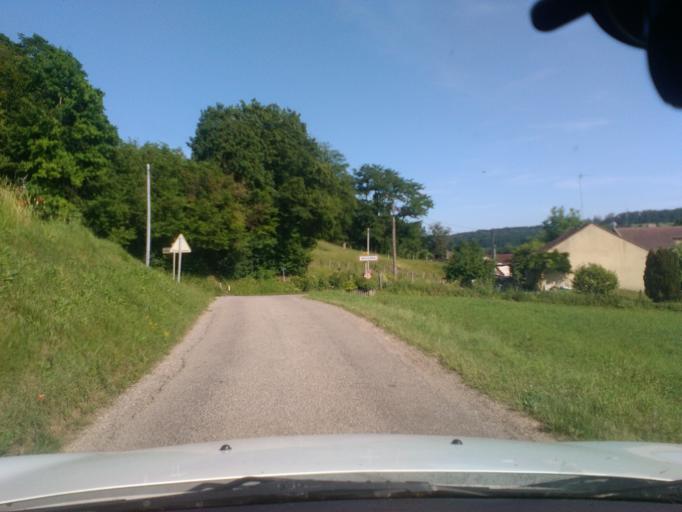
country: FR
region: Lorraine
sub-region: Departement des Vosges
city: Mirecourt
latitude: 48.3151
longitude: 6.2085
